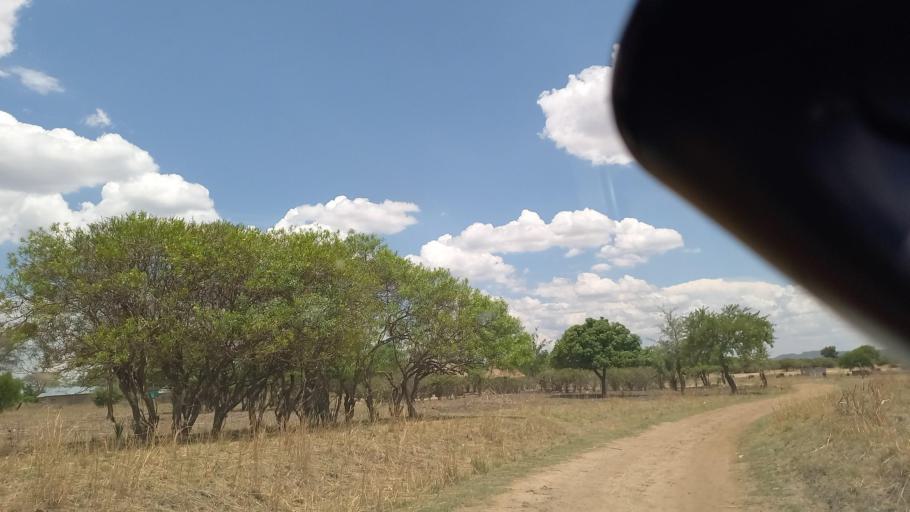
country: ZM
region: Southern
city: Mazabuka
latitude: -16.1140
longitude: 27.8124
